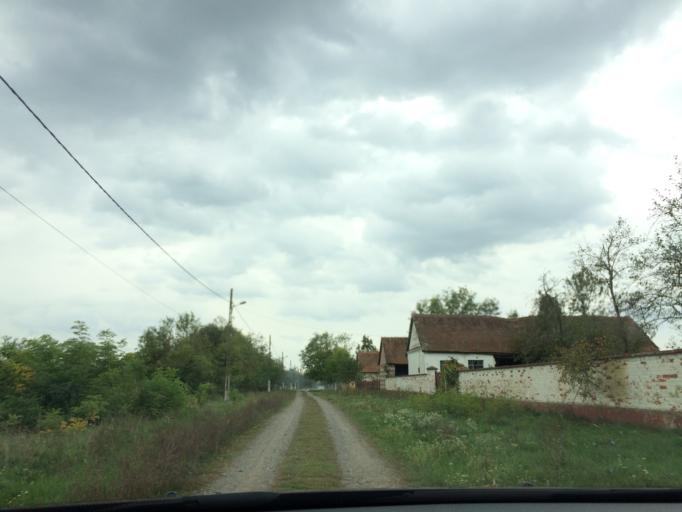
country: RO
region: Timis
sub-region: Oras Recas
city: Recas
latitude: 45.7397
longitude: 21.4991
